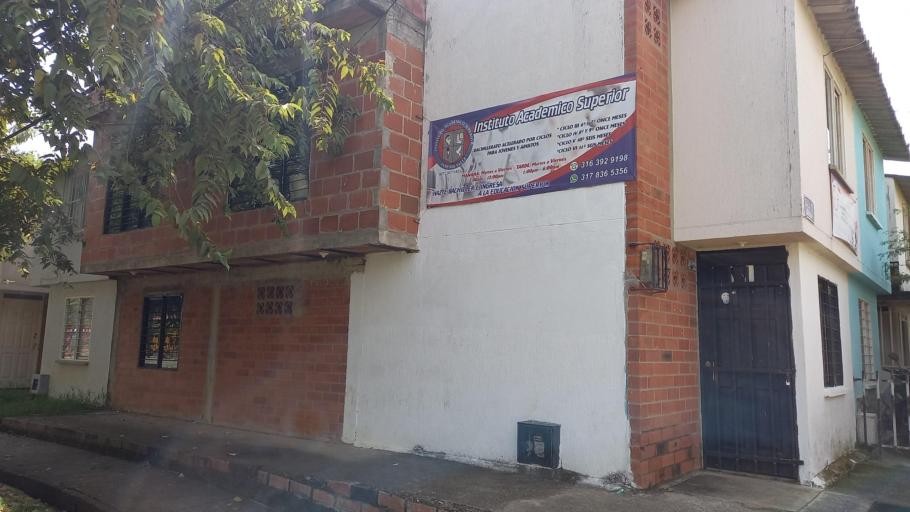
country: CO
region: Valle del Cauca
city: Jamundi
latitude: 3.2408
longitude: -76.5127
